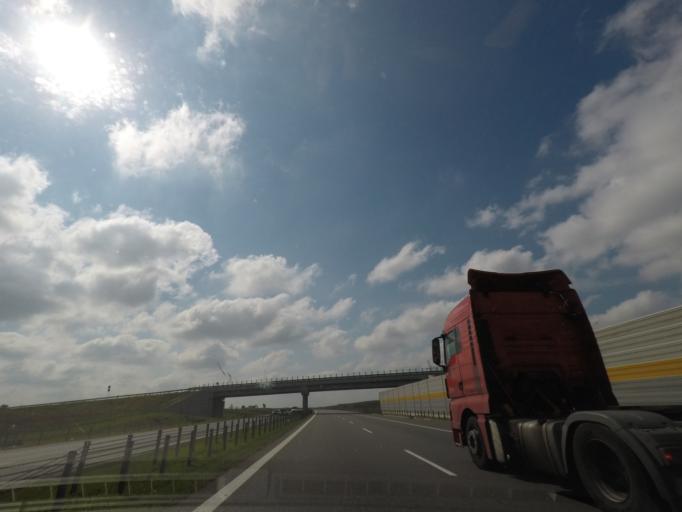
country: PL
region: Kujawsko-Pomorskie
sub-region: Powiat chelminski
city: Lisewo
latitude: 53.2309
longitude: 18.7269
